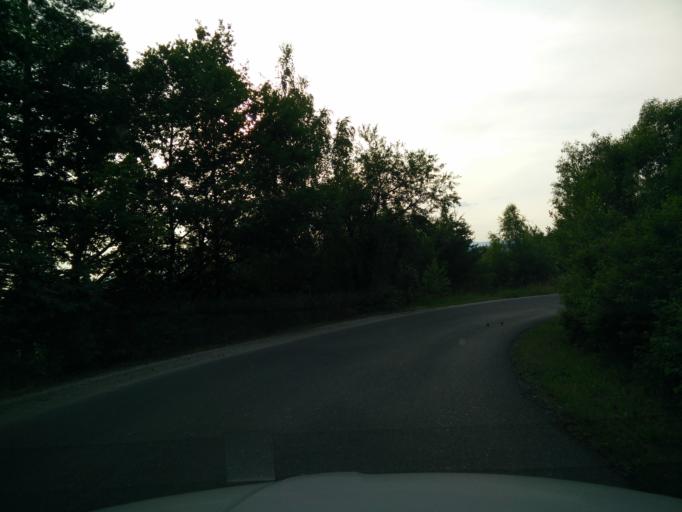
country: SK
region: Nitriansky
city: Prievidza
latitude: 48.7395
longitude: 18.6342
